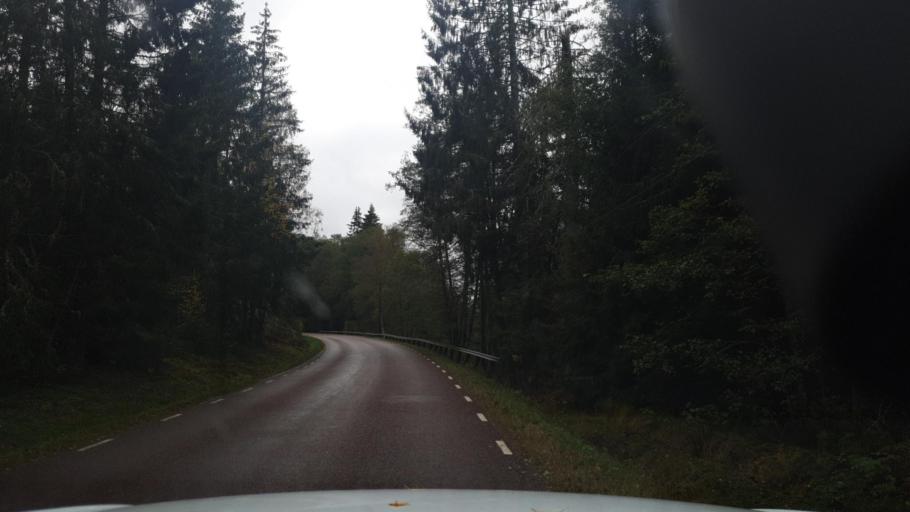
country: SE
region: Vaermland
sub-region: Grums Kommun
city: Grums
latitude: 59.4092
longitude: 13.0724
